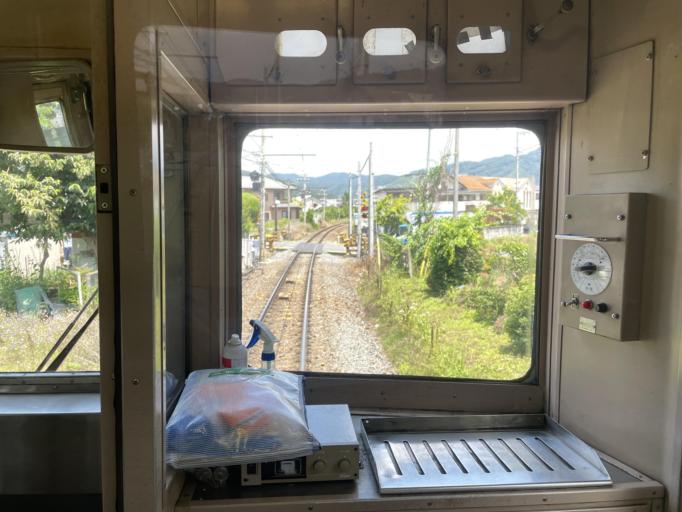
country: JP
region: Saitama
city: Chichibu
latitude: 36.0745
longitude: 139.0968
